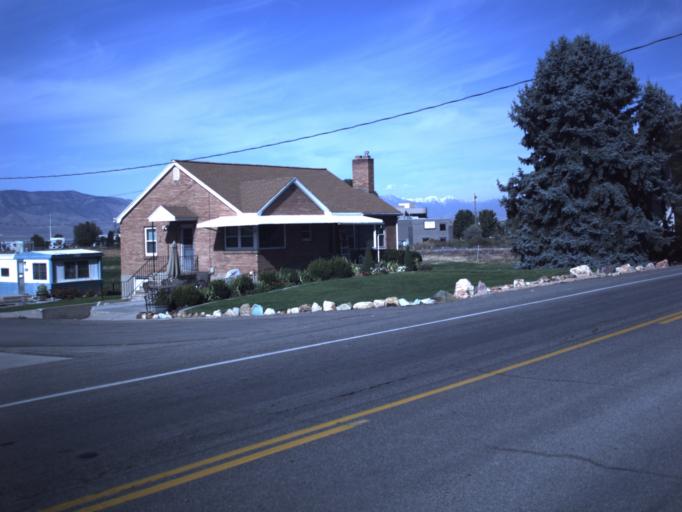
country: US
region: Utah
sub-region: Utah County
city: Orem
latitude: 40.2727
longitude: -111.7252
